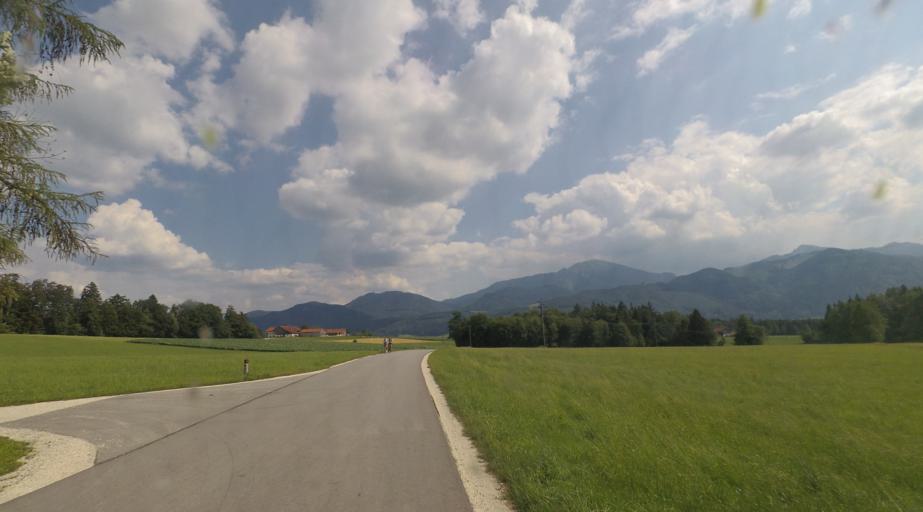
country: DE
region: Bavaria
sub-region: Upper Bavaria
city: Grabenstatt
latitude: 47.8236
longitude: 12.5522
